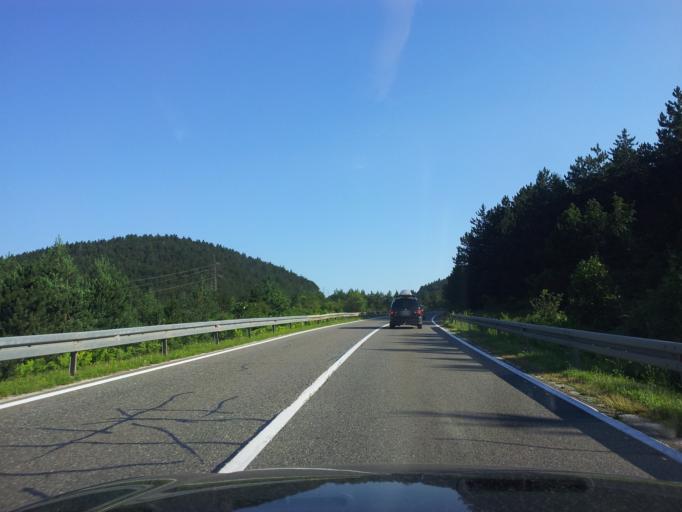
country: HR
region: Licko-Senjska
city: Jezerce
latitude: 44.7857
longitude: 15.6865
